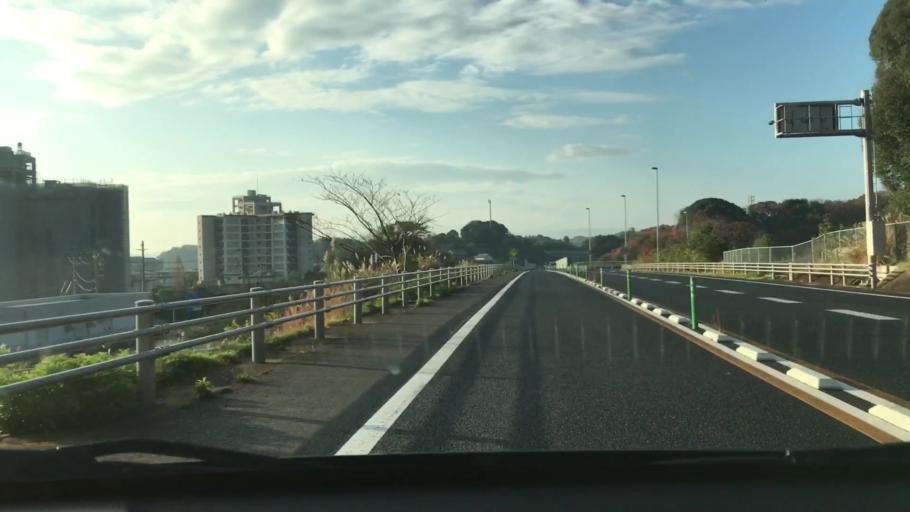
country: JP
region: Nagasaki
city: Sasebo
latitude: 33.0867
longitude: 129.7778
